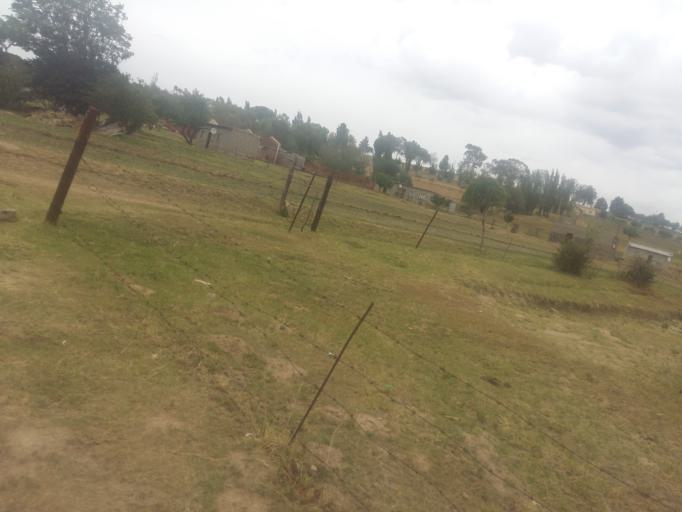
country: LS
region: Mafeteng
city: Mafeteng
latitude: -29.6957
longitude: 27.4374
